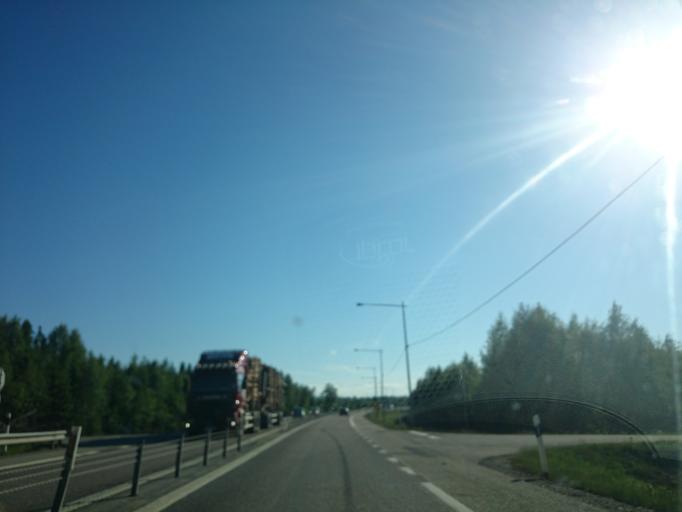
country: SE
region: Vaesternorrland
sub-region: Timra Kommun
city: Soraker
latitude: 62.5186
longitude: 17.4644
